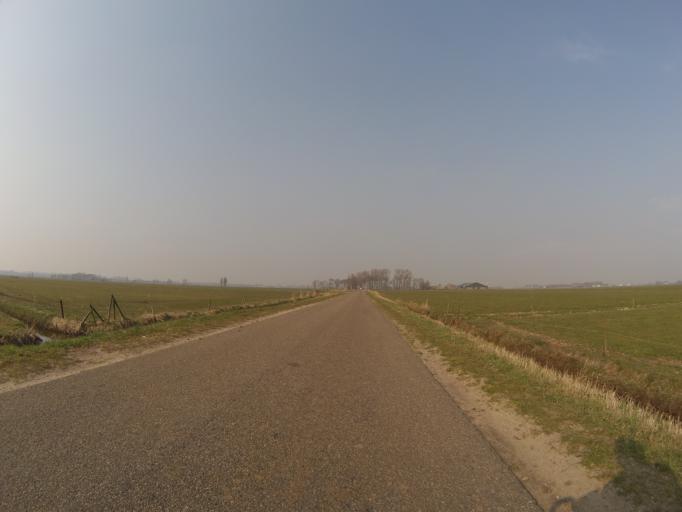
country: NL
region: Utrecht
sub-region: Gemeente Amersfoort
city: Hoogland
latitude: 52.1987
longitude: 5.3331
